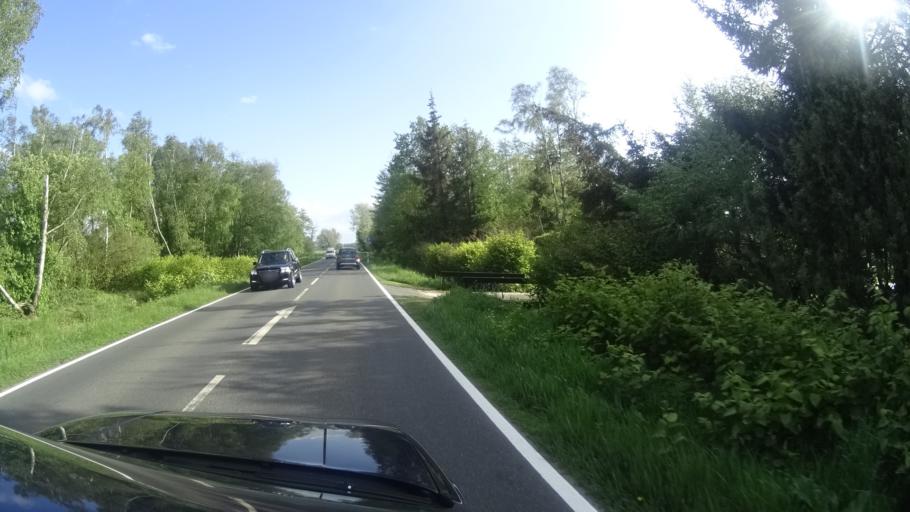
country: DE
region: Mecklenburg-Vorpommern
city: Ostseebad Dierhagen
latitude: 54.3074
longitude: 12.3540
